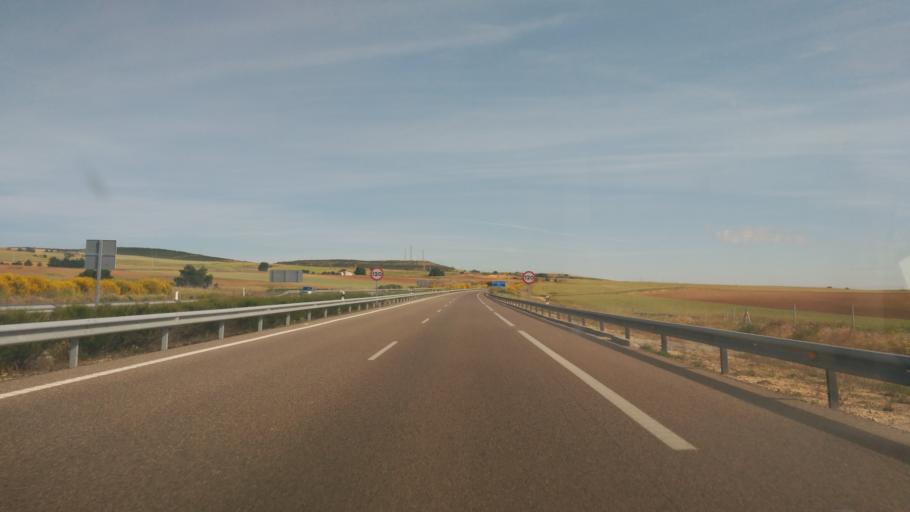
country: ES
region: Castille and Leon
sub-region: Provincia de Zamora
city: Corrales
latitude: 41.3671
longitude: -5.7163
